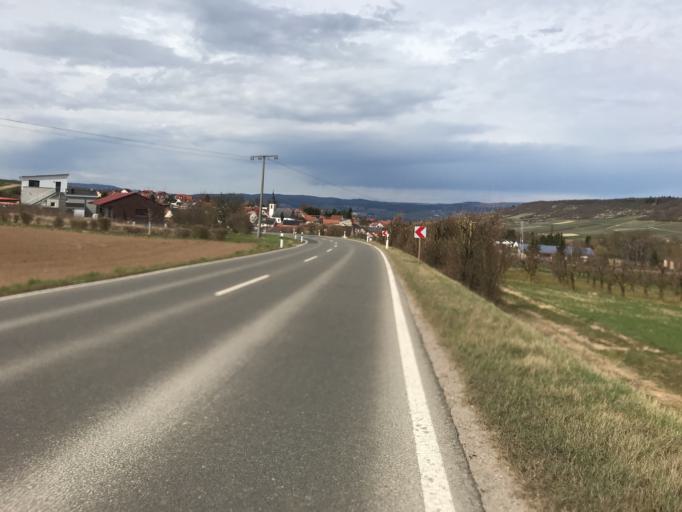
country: DE
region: Rheinland-Pfalz
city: Appenheim
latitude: 49.9272
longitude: 8.0394
